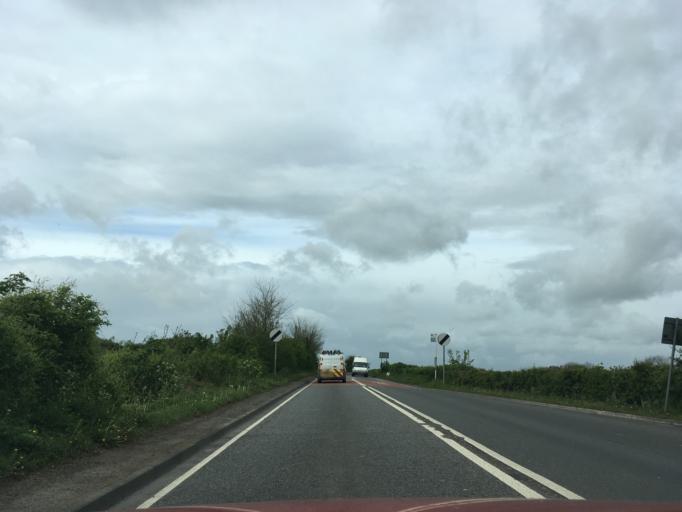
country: GB
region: England
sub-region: Bath and North East Somerset
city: Wellow
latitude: 51.3494
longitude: -2.3922
